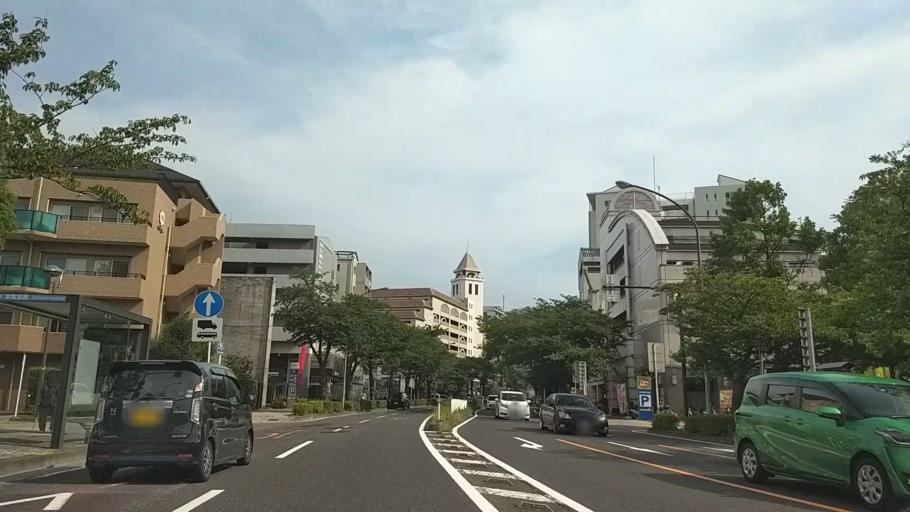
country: JP
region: Kanagawa
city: Yokohama
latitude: 35.4277
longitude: 139.6656
